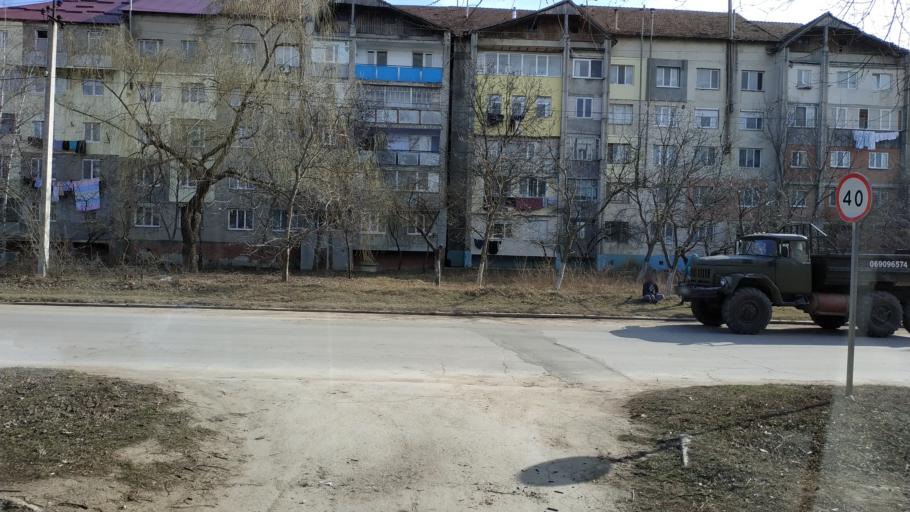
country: MD
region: Nisporeni
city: Nisporeni
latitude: 47.0744
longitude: 28.1810
